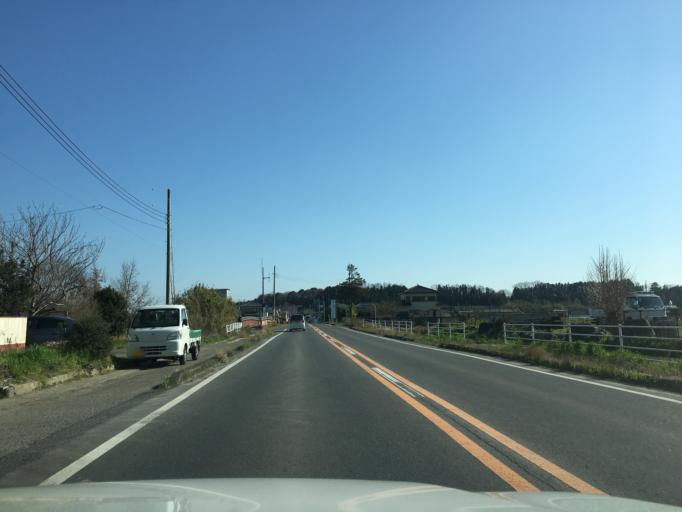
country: JP
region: Ibaraki
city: Omiya
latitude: 36.4481
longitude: 140.4098
